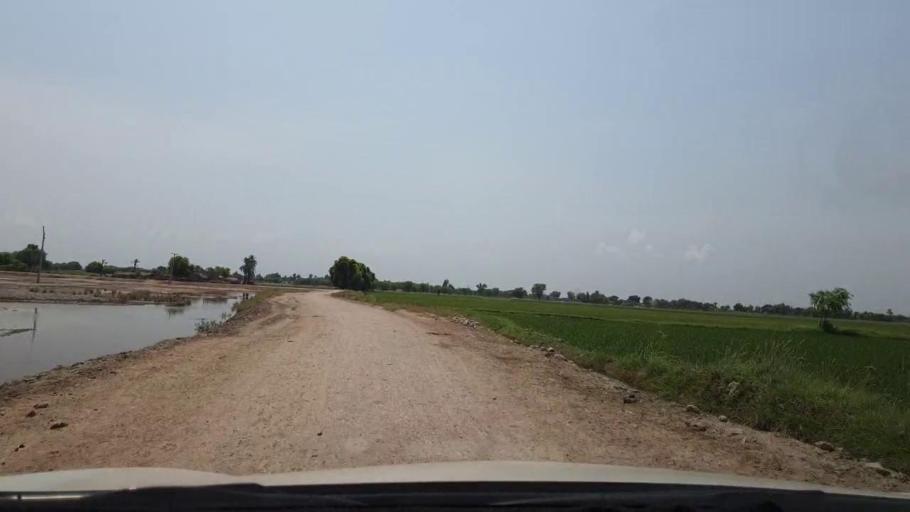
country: PK
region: Sindh
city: Ratodero
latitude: 27.8108
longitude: 68.2428
